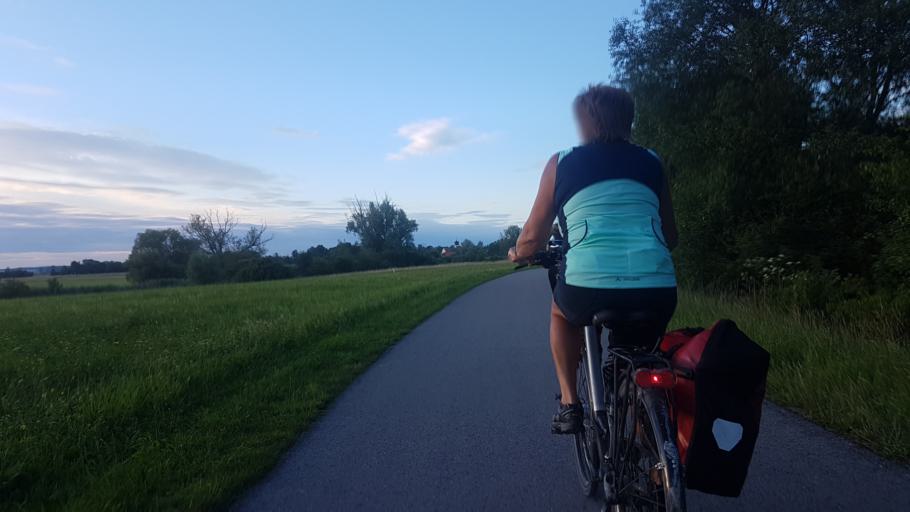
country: DE
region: Bavaria
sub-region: Regierungsbezirk Mittelfranken
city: Muhr am See
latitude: 49.1455
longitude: 10.7018
